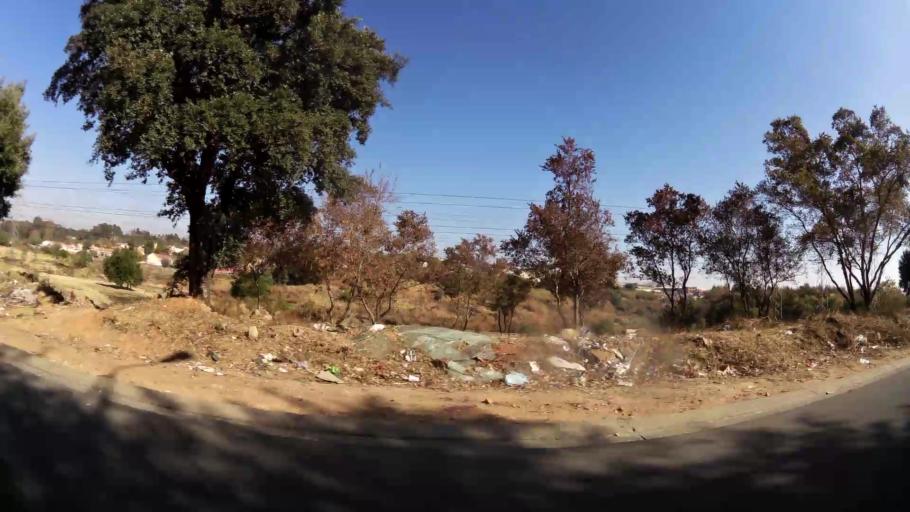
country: ZA
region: Gauteng
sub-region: City of Johannesburg Metropolitan Municipality
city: Modderfontein
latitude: -26.1145
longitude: 28.1150
